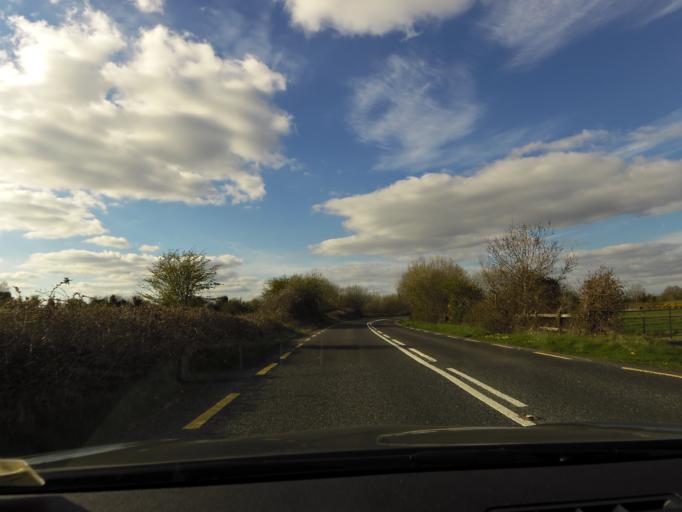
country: IE
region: Connaught
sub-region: County Galway
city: Portumna
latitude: 53.1279
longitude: -8.2453
